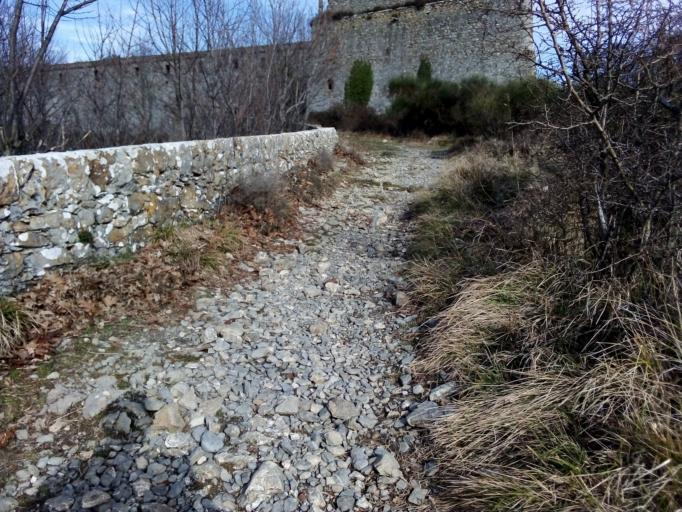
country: IT
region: Liguria
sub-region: Provincia di Genova
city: Piccarello
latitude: 44.4327
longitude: 8.9983
